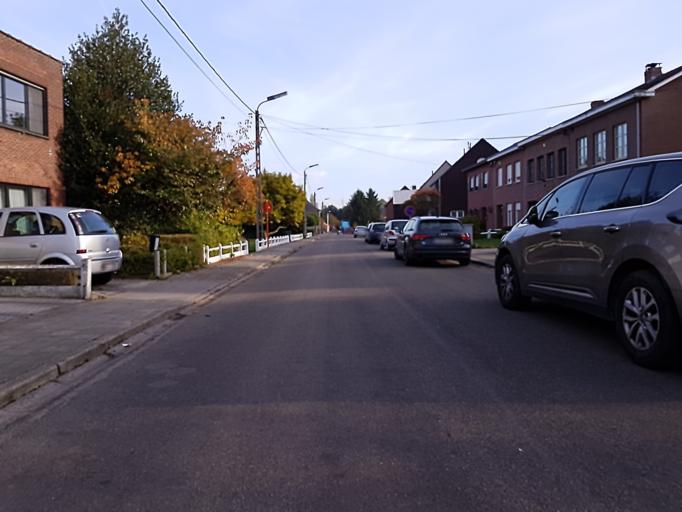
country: BE
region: Flanders
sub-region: Provincie Antwerpen
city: Mechelen
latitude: 51.0559
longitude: 4.4867
